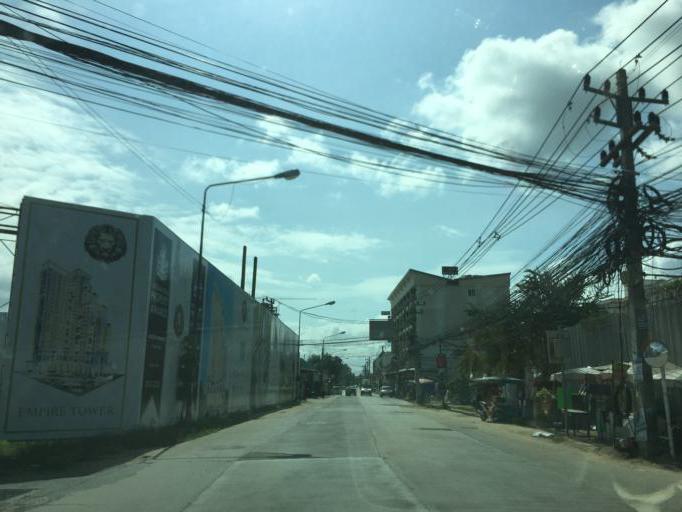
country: TH
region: Chon Buri
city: Phatthaya
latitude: 12.8895
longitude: 100.8846
